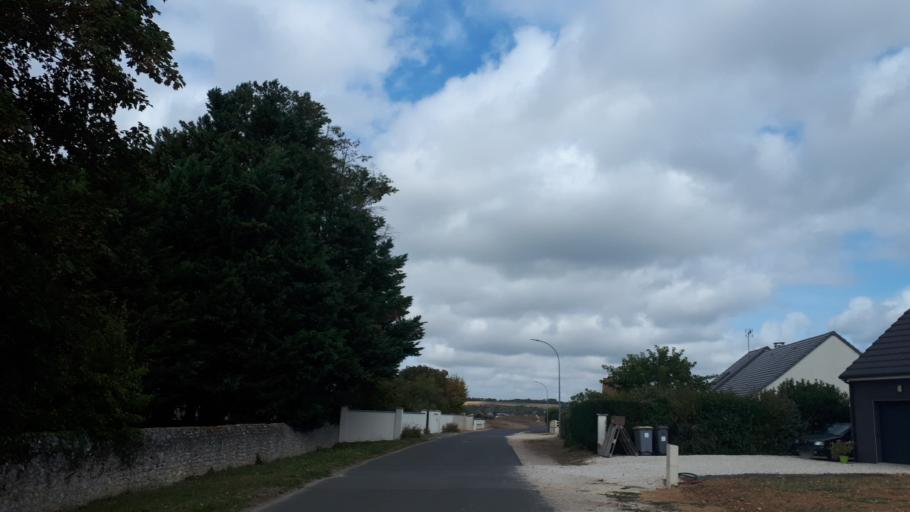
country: FR
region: Centre
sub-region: Departement du Loir-et-Cher
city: Villiers-sur-Loir
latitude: 47.7928
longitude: 0.9972
